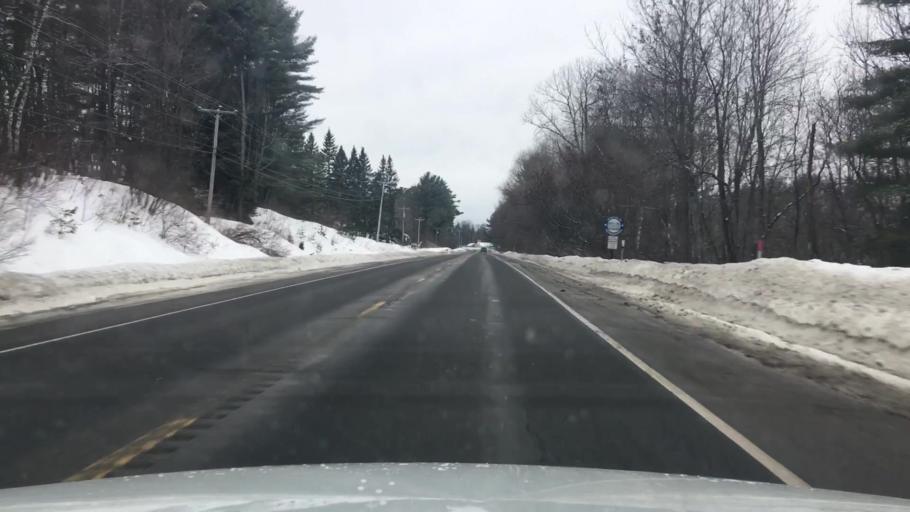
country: US
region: Maine
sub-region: Somerset County
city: Norridgewock
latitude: 44.7249
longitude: -69.7769
